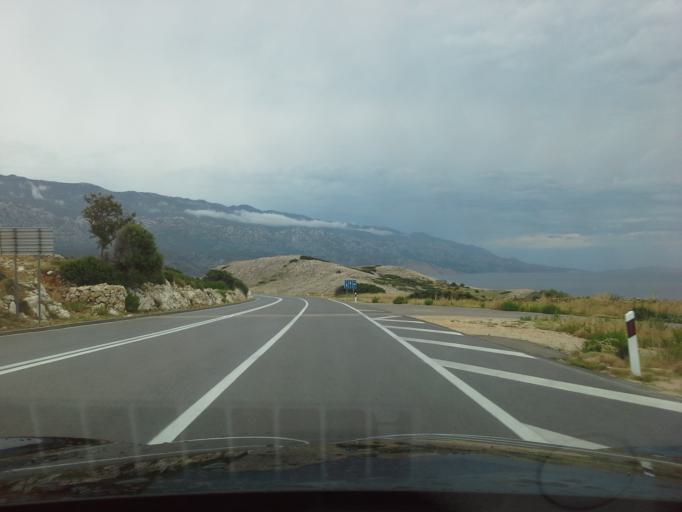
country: HR
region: Primorsko-Goranska
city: Banjol
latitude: 44.7054
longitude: 14.8444
